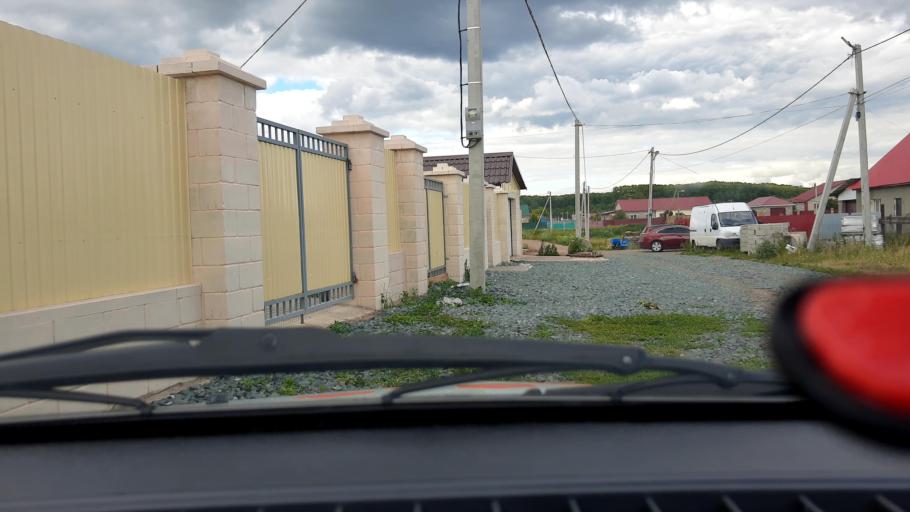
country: RU
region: Bashkortostan
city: Kabakovo
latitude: 54.5152
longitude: 55.9479
